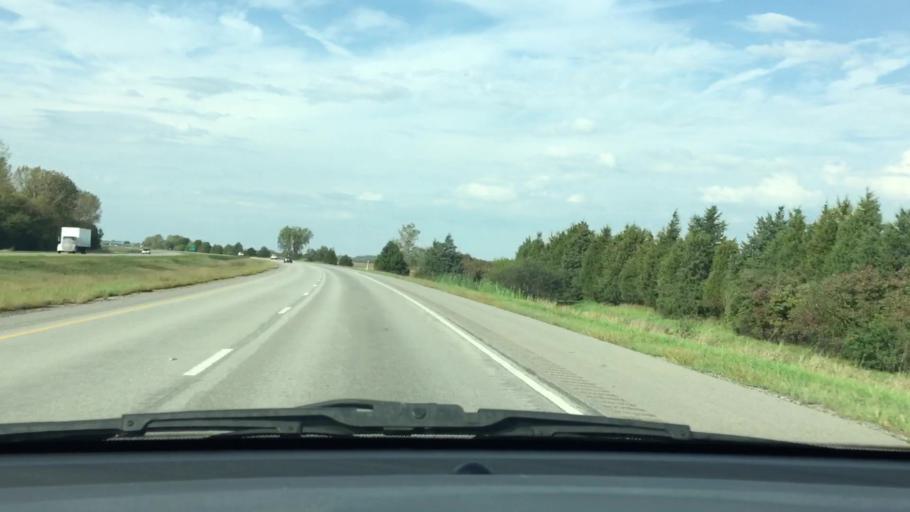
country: US
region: Iowa
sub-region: Scott County
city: Le Claire
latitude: 41.5417
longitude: -90.2819
